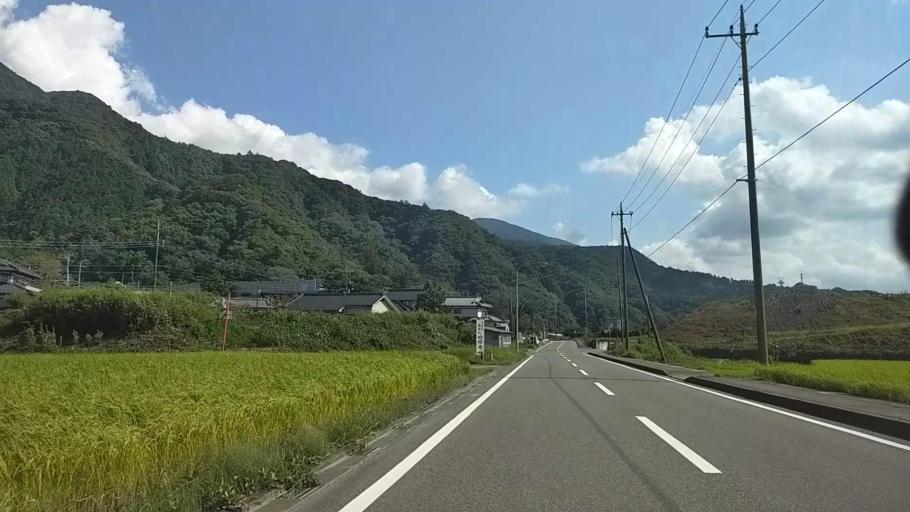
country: JP
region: Shizuoka
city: Fujinomiya
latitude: 35.3871
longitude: 138.4529
